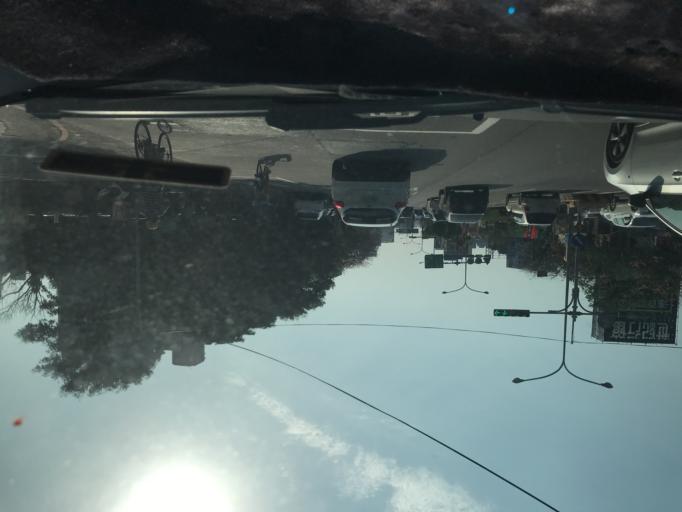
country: TW
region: Taiwan
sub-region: Hsinchu
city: Zhubei
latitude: 24.8182
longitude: 121.0268
